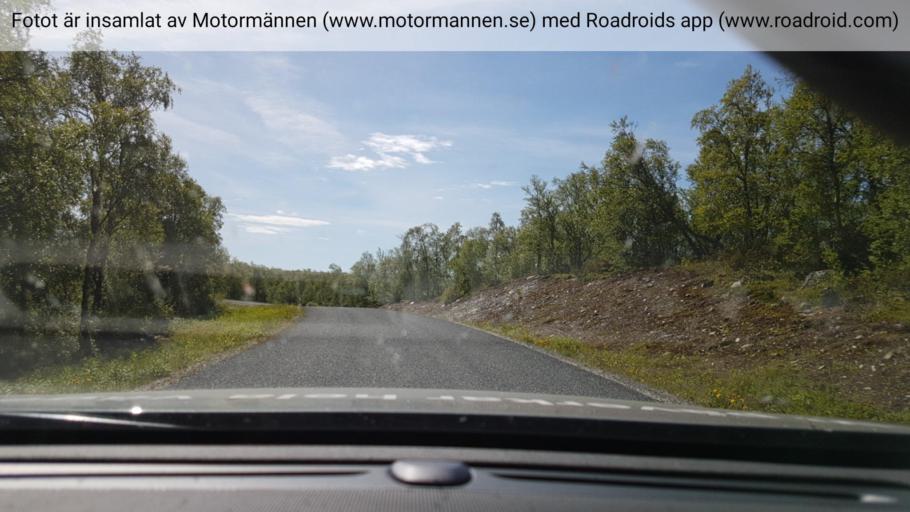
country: NO
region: Nordland
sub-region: Hattfjelldal
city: Hattfjelldal
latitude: 65.3795
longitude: 15.0264
